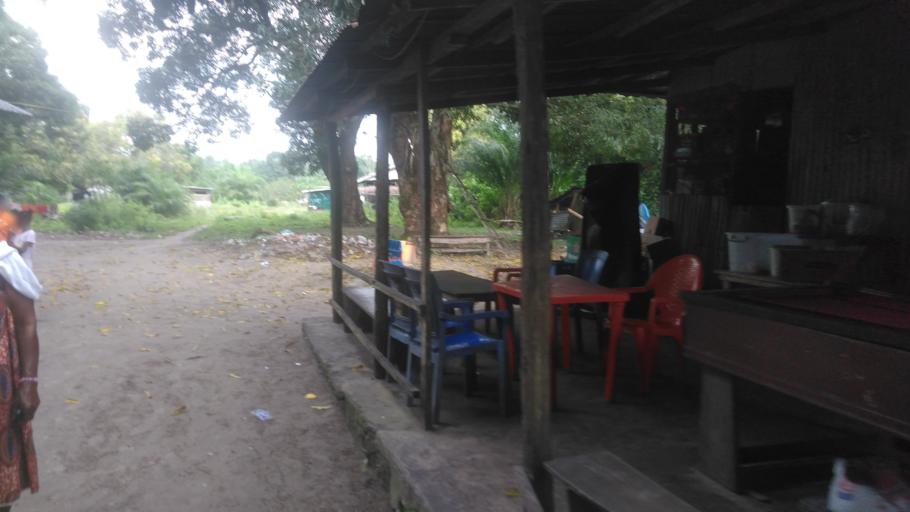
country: NG
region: Delta
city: Sapele
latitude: 5.8413
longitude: 5.1261
